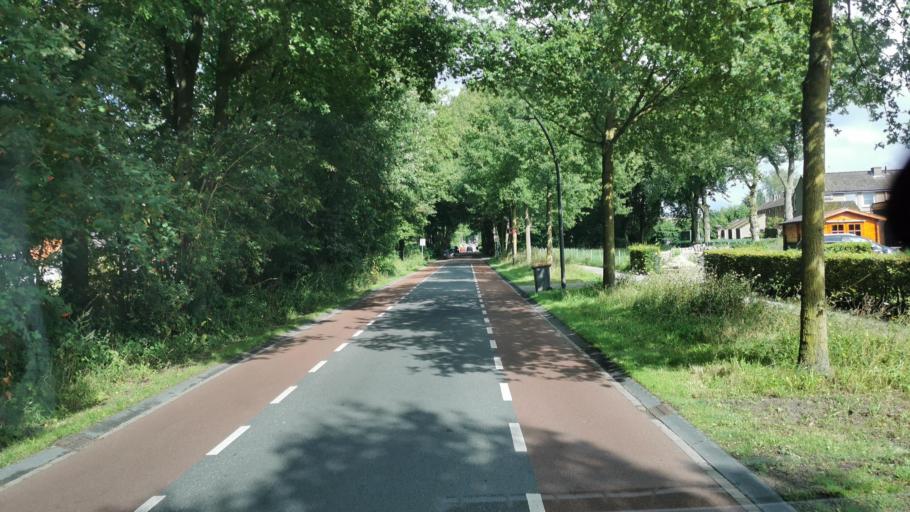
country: NL
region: Overijssel
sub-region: Gemeente Losser
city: Losser
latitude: 52.3100
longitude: 6.9898
